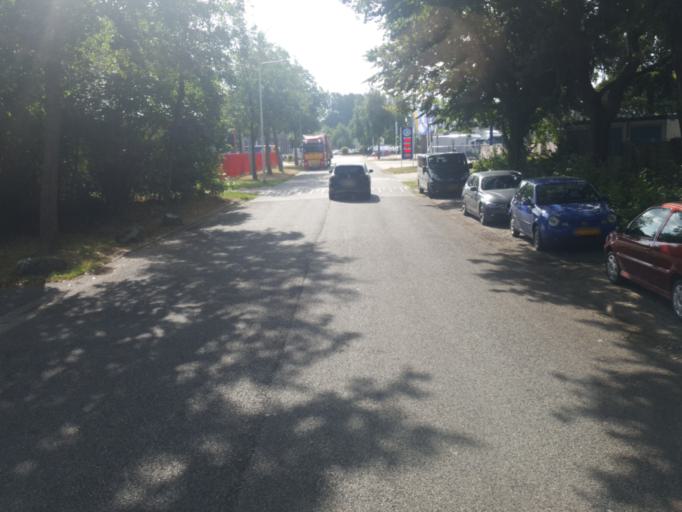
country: NL
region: Gelderland
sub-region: Gemeente Doetinchem
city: Doetinchem
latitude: 51.9682
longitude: 6.2670
